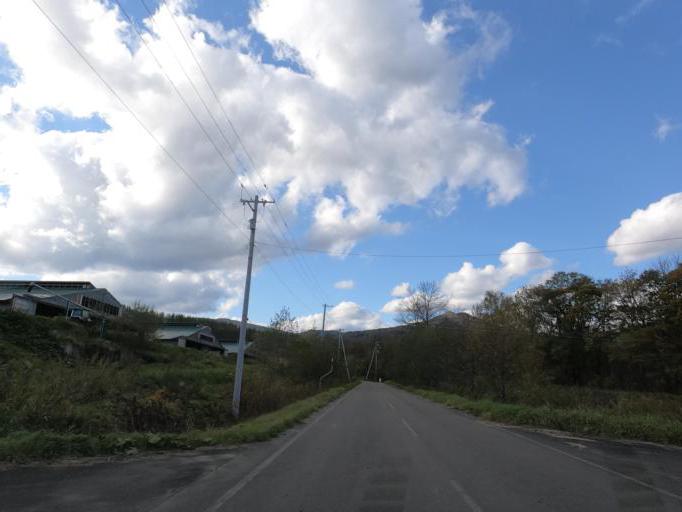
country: JP
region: Hokkaido
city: Otofuke
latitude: 43.2902
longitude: 143.2281
